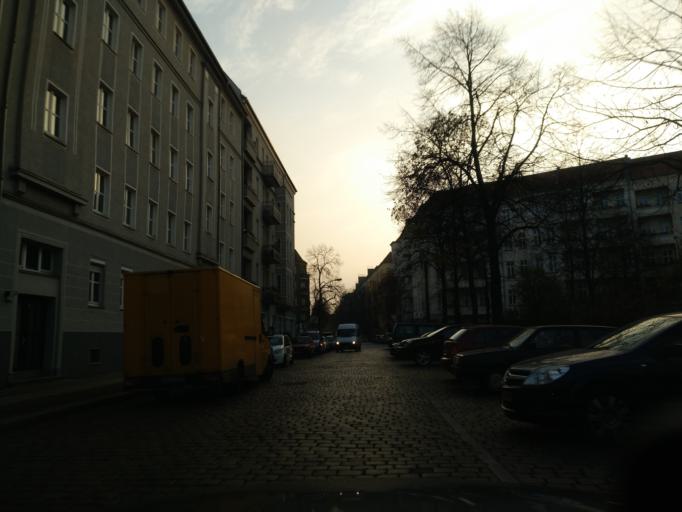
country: DE
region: Berlin
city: Friedrichshain Bezirk
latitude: 52.5105
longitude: 13.4650
